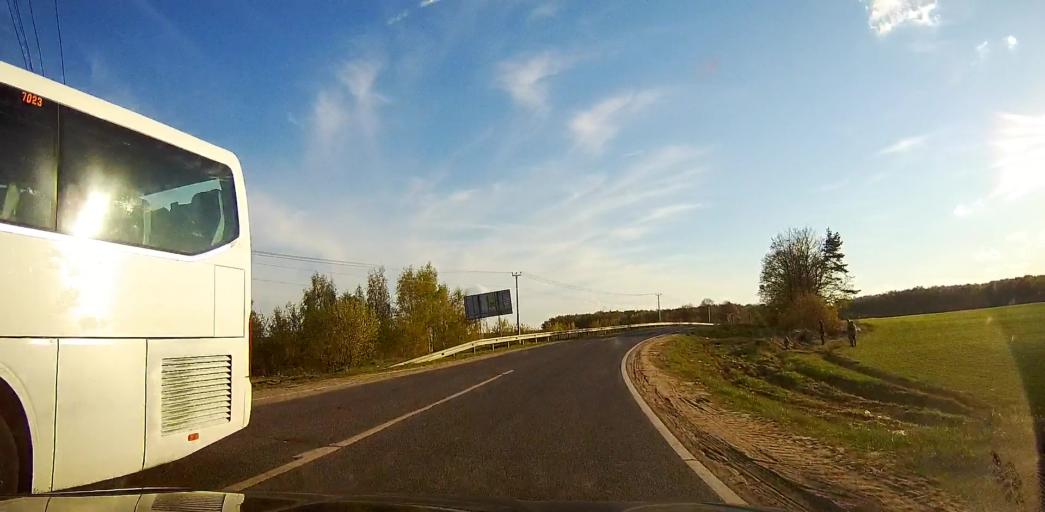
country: RU
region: Moskovskaya
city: Bronnitsy
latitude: 55.2957
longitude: 38.2121
